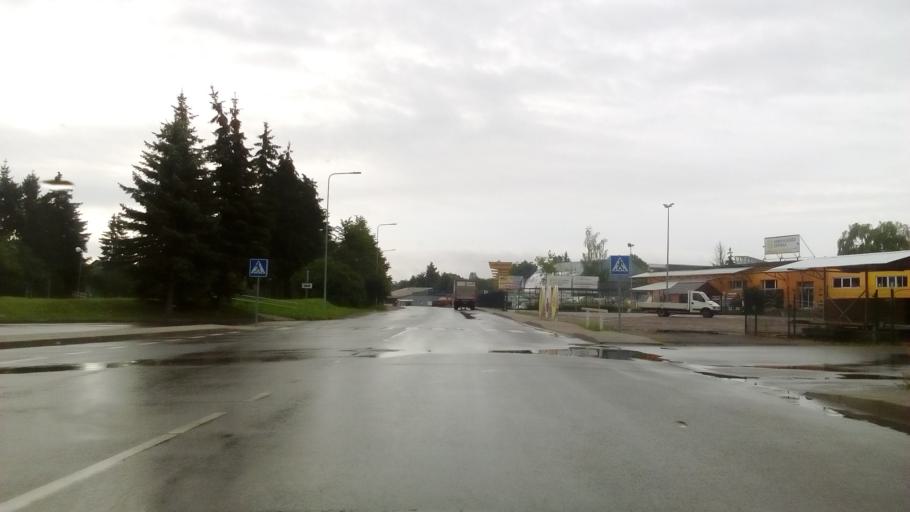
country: LT
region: Alytaus apskritis
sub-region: Alytus
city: Alytus
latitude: 54.3918
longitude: 24.0369
